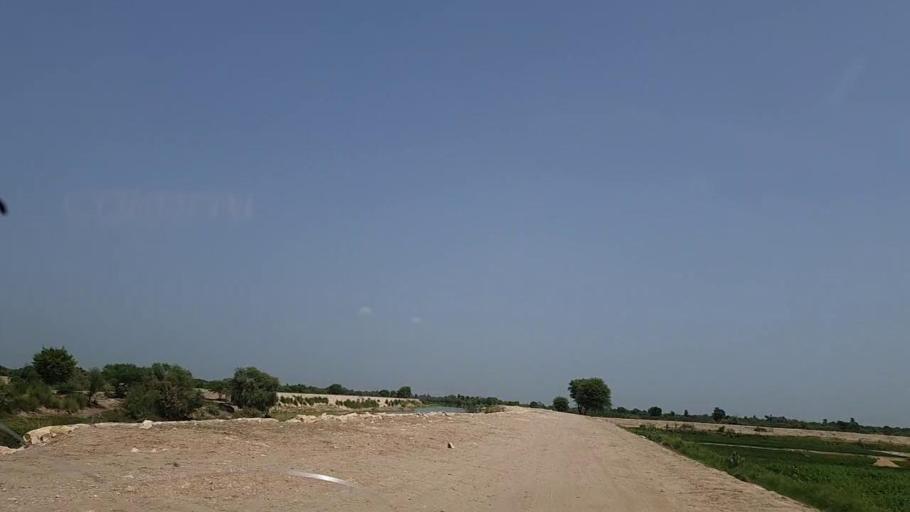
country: PK
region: Sindh
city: Kandiaro
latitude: 27.0567
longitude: 68.1339
